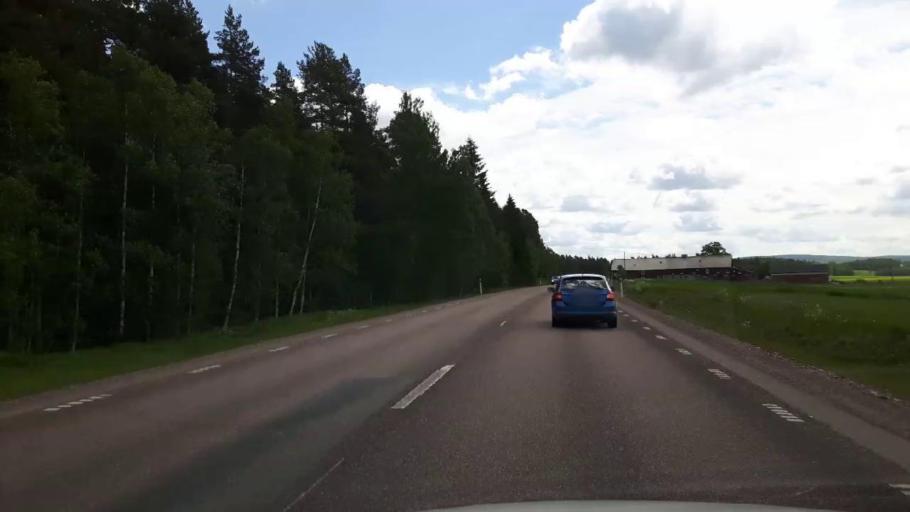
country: SE
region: Dalarna
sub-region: Saters Kommun
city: Saeter
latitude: 60.4384
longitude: 15.8205
